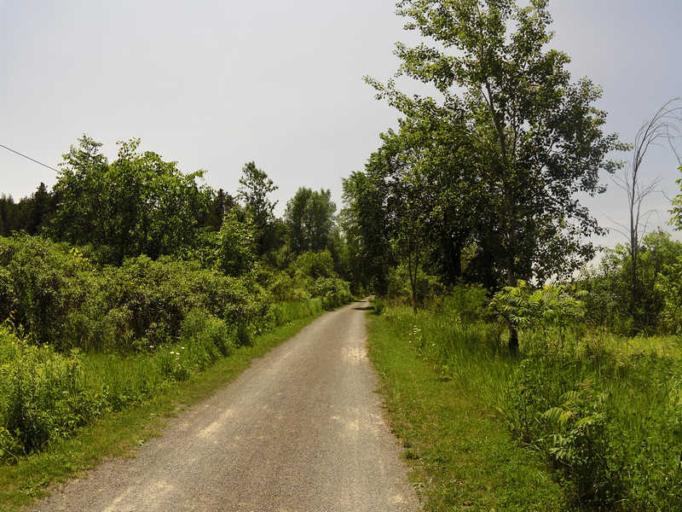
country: CA
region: Ontario
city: Peterborough
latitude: 44.4093
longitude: -78.2616
